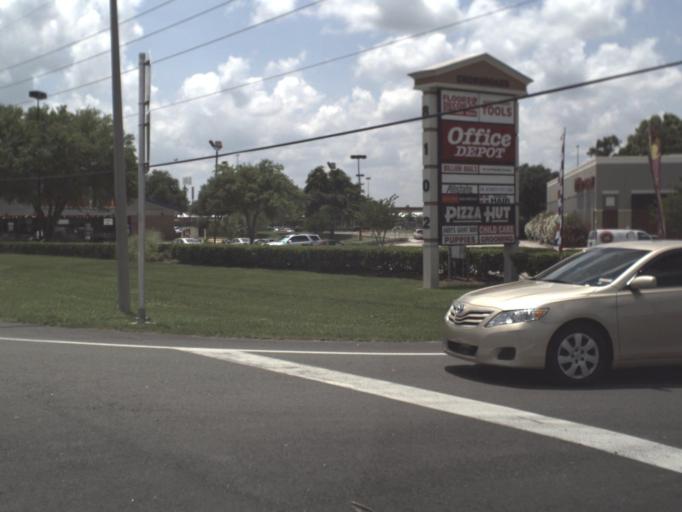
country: US
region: Florida
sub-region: Clay County
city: Bellair-Meadowbrook Terrace
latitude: 30.2011
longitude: -81.7396
